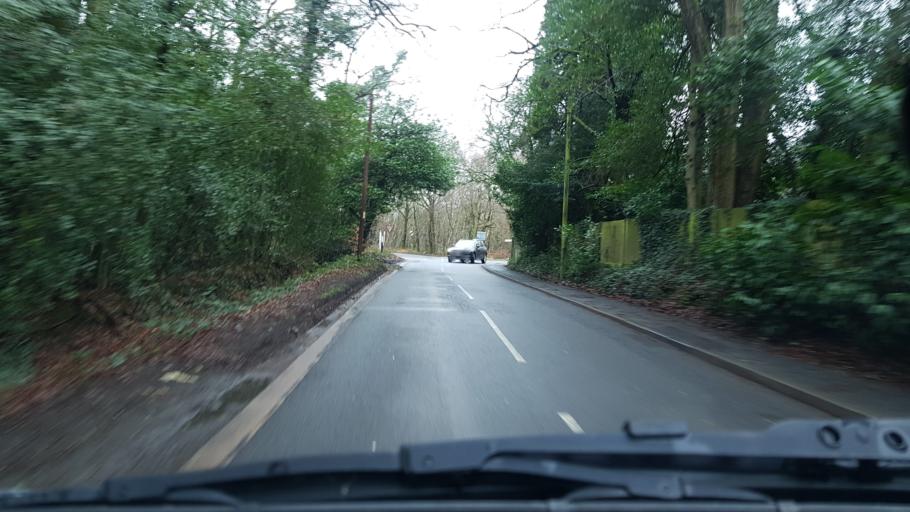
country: GB
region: England
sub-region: Surrey
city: Hindhead
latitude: 51.0945
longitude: -0.7543
